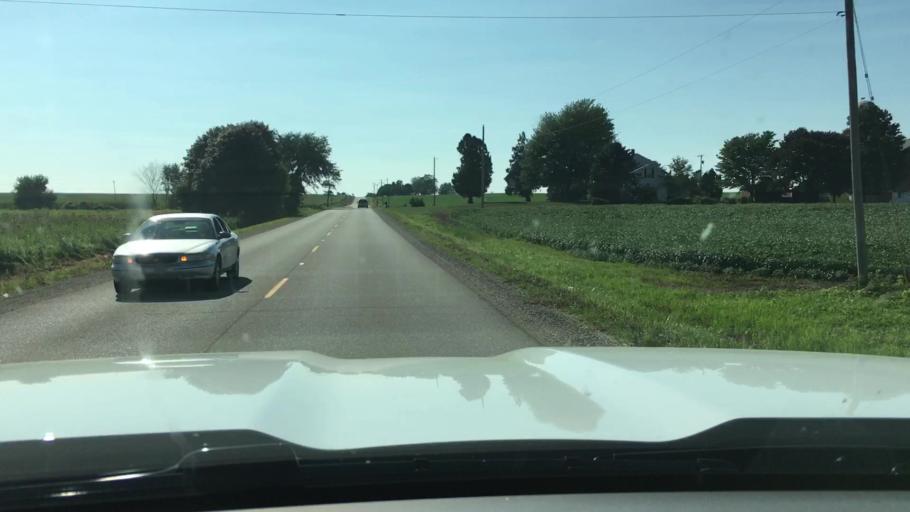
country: US
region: Michigan
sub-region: Ottawa County
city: Coopersville
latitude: 43.0747
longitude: -85.9524
